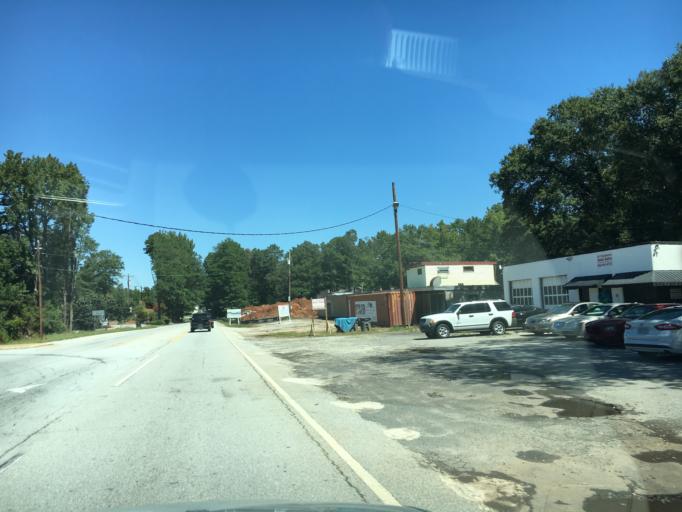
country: US
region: South Carolina
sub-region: Greenville County
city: Gantt
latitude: 34.8070
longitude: -82.4220
